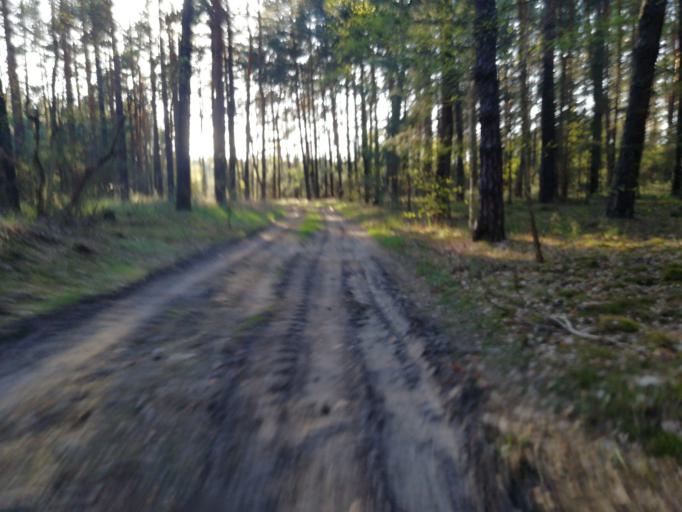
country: DE
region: Brandenburg
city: Calau
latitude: 51.7313
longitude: 14.0032
